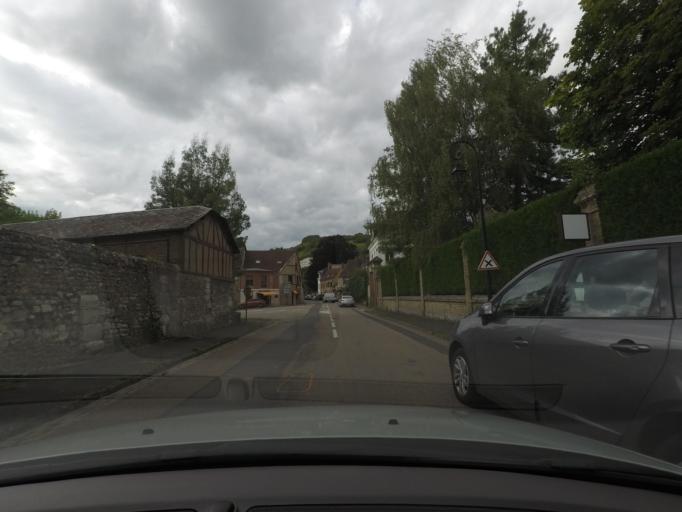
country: FR
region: Haute-Normandie
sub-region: Departement de l'Eure
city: Les Andelys
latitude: 49.2436
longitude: 1.3990
